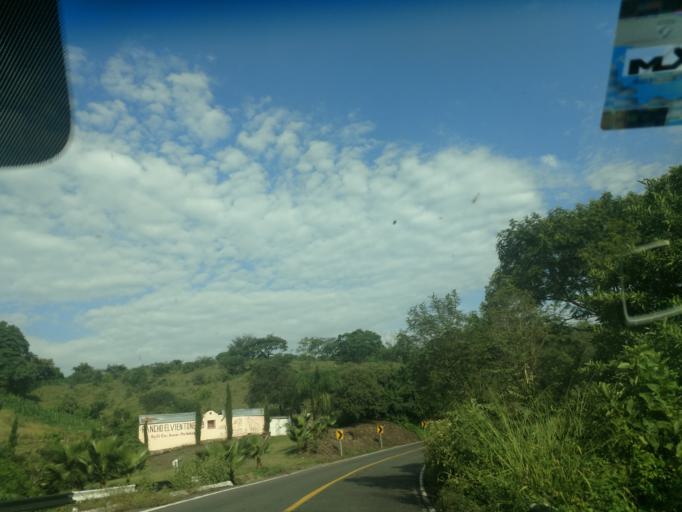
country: MX
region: Jalisco
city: Ameca
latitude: 20.5220
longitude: -104.1262
